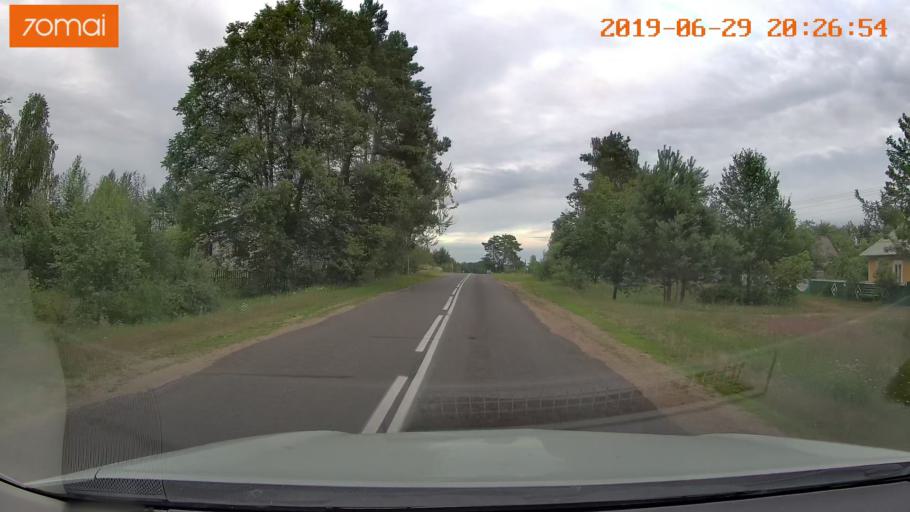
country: BY
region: Brest
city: Hantsavichy
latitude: 52.4703
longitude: 26.2999
